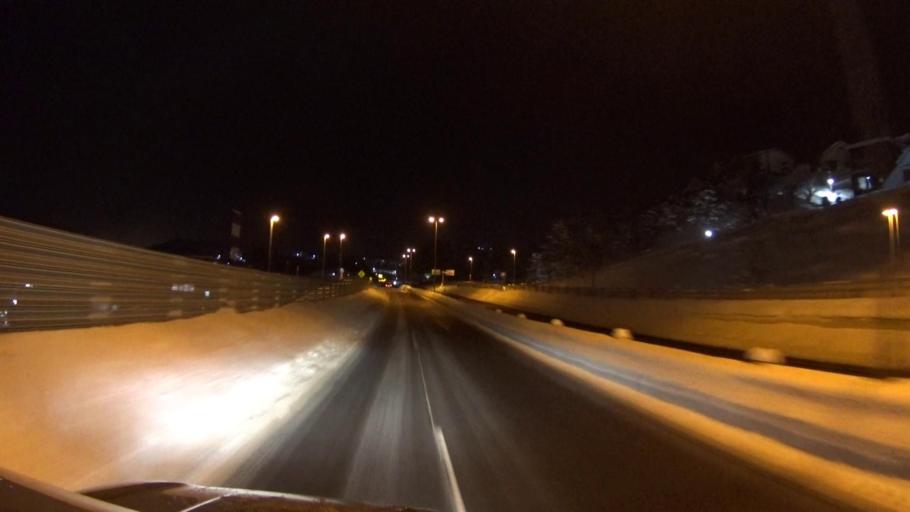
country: JP
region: Hokkaido
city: Otaru
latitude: 43.1811
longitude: 141.0204
